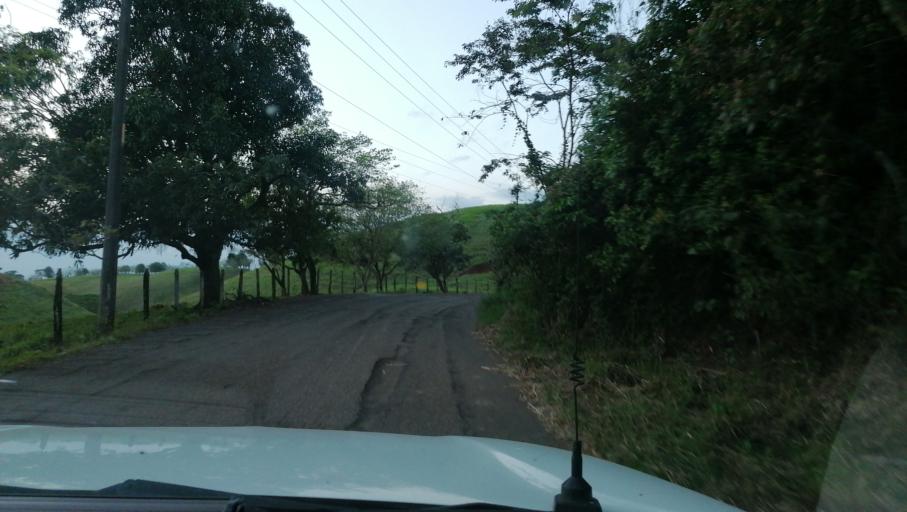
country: MX
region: Chiapas
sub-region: Ostuacan
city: Nuevo Juan del Grijalva
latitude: 17.4308
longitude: -93.3522
